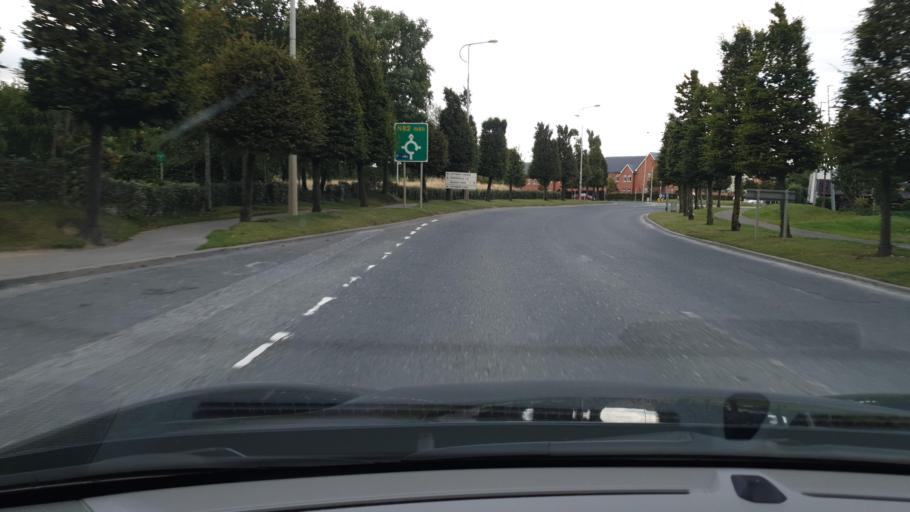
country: IE
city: Jobstown
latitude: 53.2887
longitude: -6.4240
